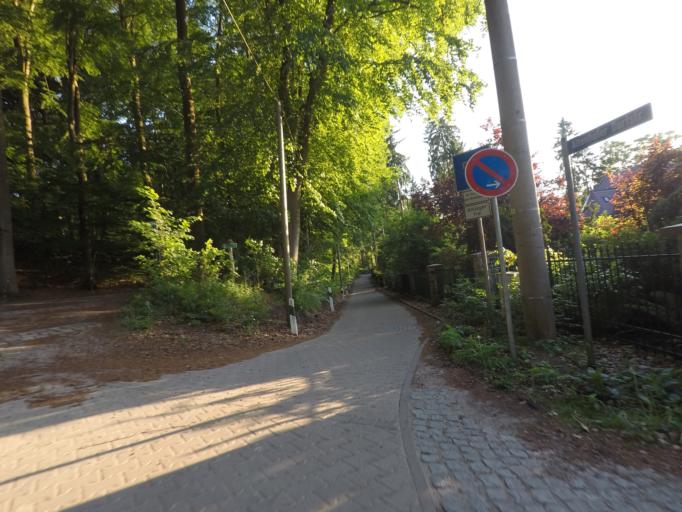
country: DE
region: Brandenburg
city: Joachimsthal
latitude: 52.9106
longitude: 13.7038
